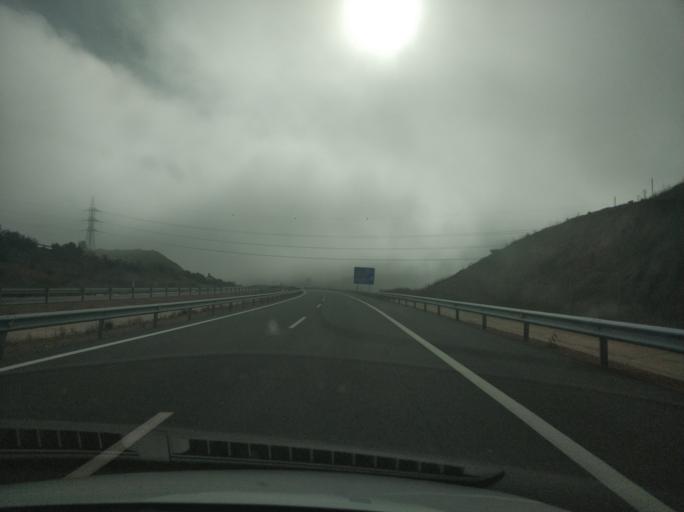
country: ES
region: Castille and Leon
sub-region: Provincia de Soria
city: Yelo
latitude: 41.2319
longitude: -2.4782
